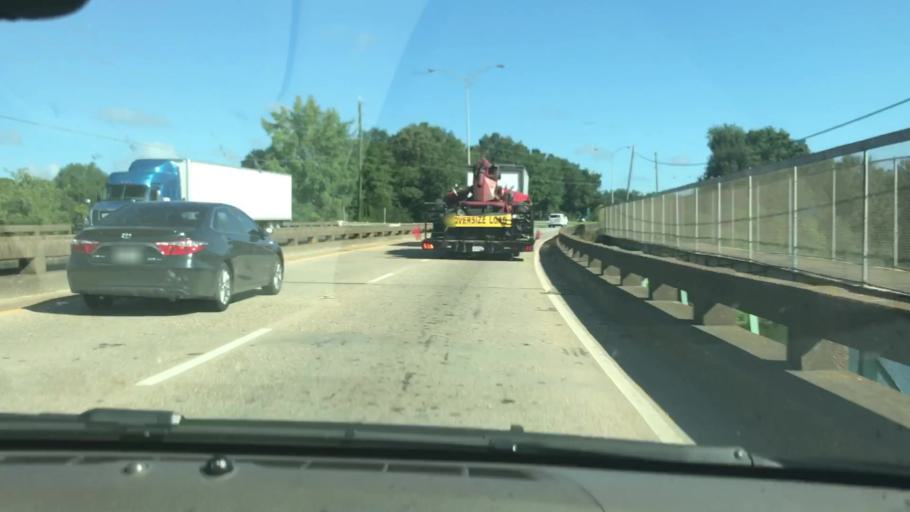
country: US
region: Alabama
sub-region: Barbour County
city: Eufaula
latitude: 31.9068
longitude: -85.1493
